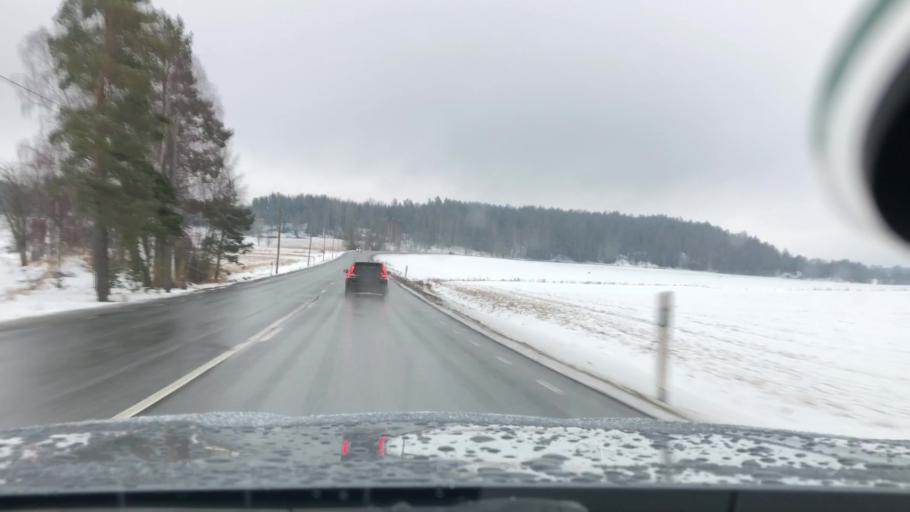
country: SE
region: Stockholm
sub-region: Sodertalje Kommun
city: Pershagen
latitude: 59.0624
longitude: 17.6090
